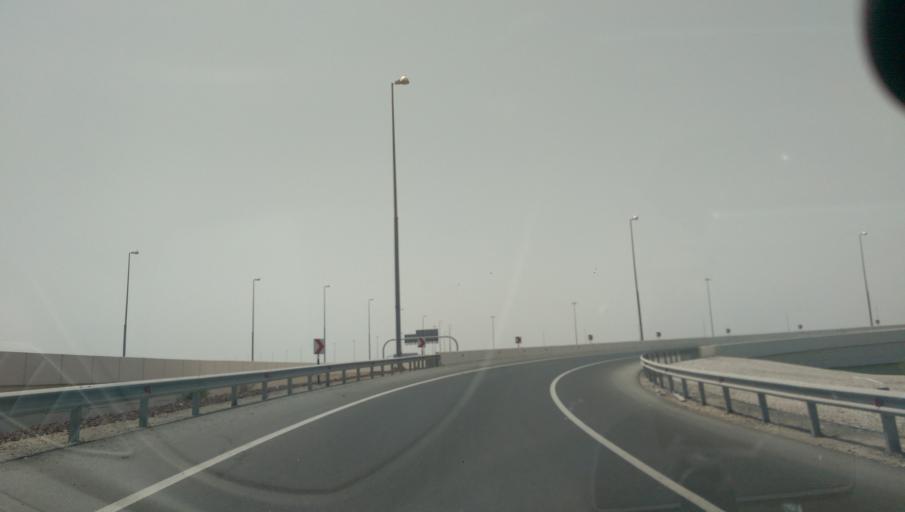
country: AE
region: Abu Dhabi
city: Abu Dhabi
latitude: 24.6950
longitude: 54.7821
